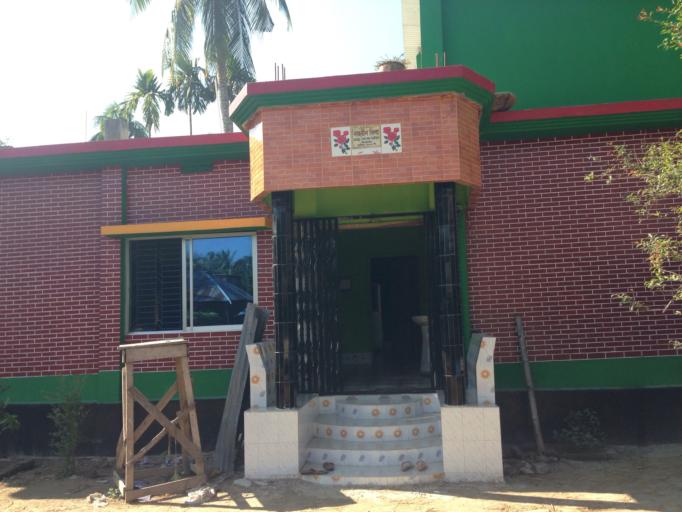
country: BD
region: Khulna
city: Kalia
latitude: 23.0537
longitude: 89.6473
